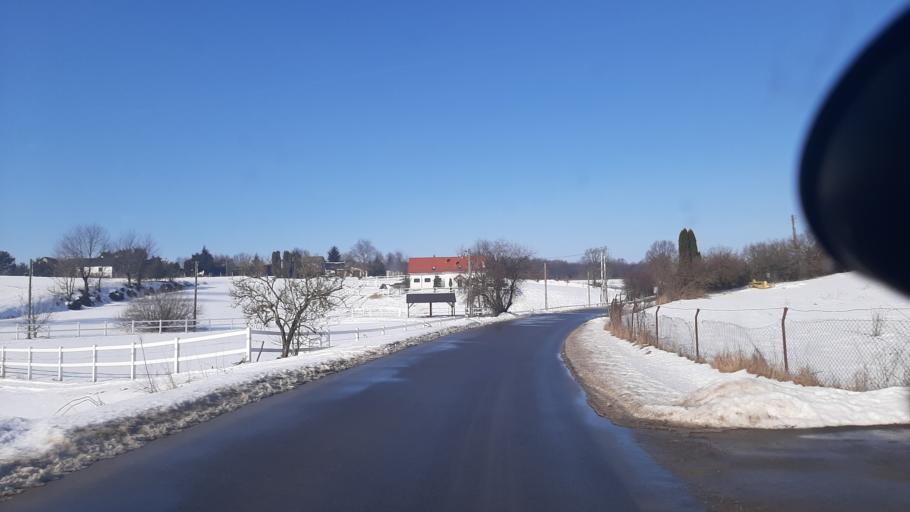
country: PL
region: Lublin Voivodeship
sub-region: Powiat pulawski
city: Naleczow
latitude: 51.2894
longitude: 22.2731
